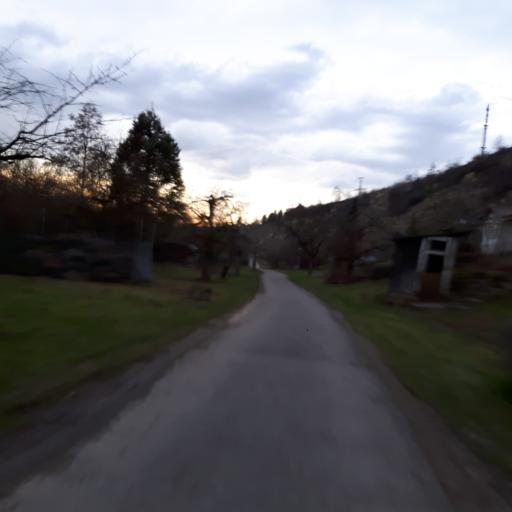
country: DE
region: Baden-Wuerttemberg
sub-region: Regierungsbezirk Stuttgart
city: Benningen am Neckar
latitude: 48.9519
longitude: 9.2373
